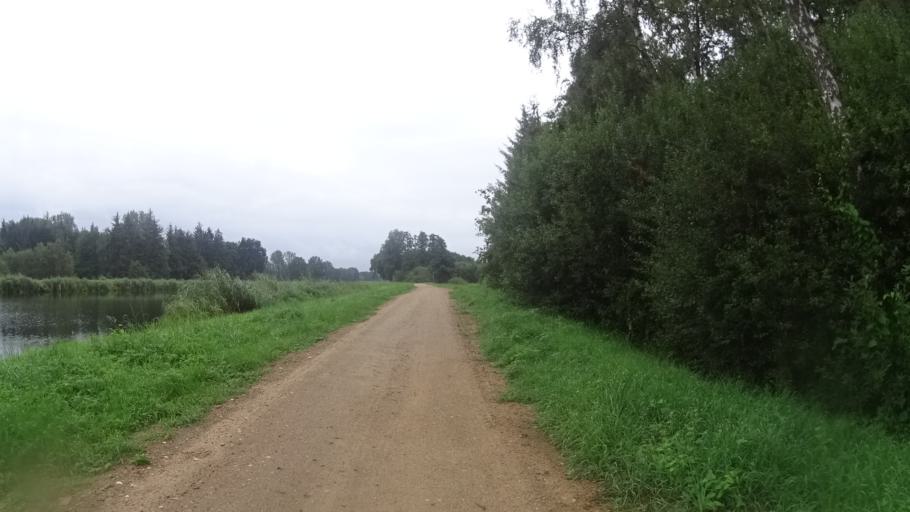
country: DE
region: Schleswig-Holstein
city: Buchen
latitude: 53.4920
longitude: 10.6295
